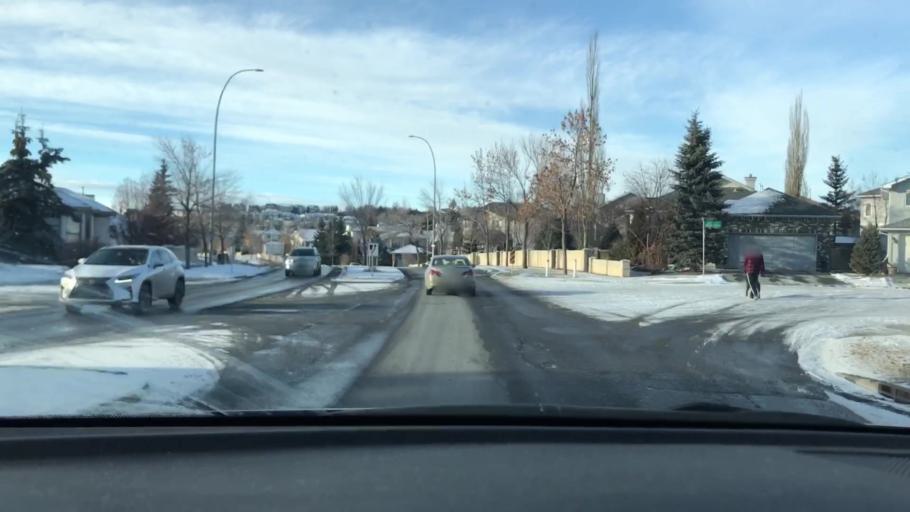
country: CA
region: Alberta
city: Calgary
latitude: 51.0201
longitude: -114.1789
